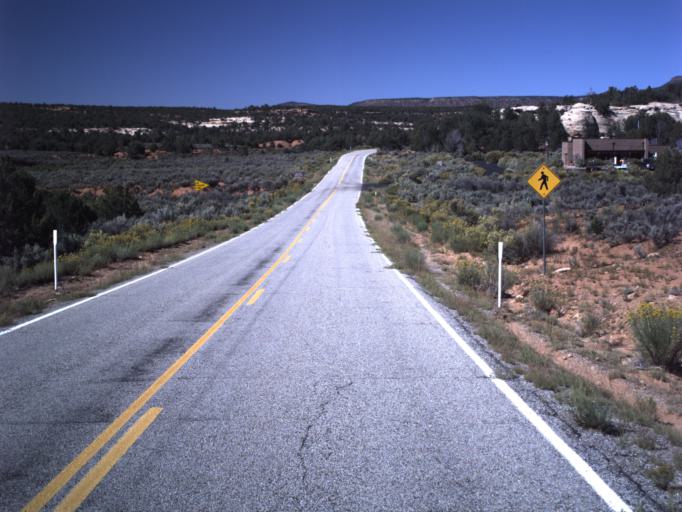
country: US
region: Utah
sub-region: San Juan County
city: Blanding
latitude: 37.5228
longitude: -109.8959
